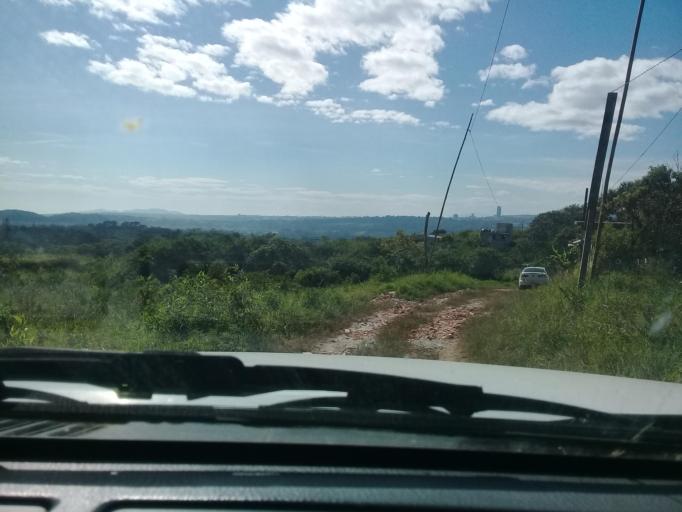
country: MX
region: Veracruz
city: El Castillo
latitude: 19.5648
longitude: -96.8792
